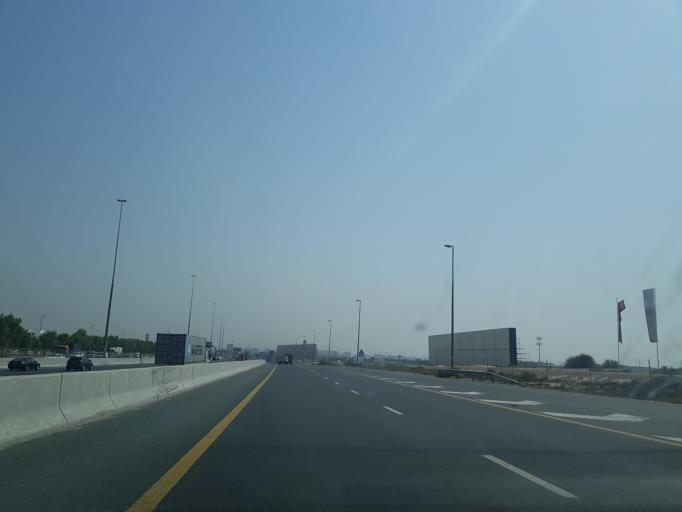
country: AE
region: Ash Shariqah
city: Sharjah
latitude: 25.1292
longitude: 55.3764
